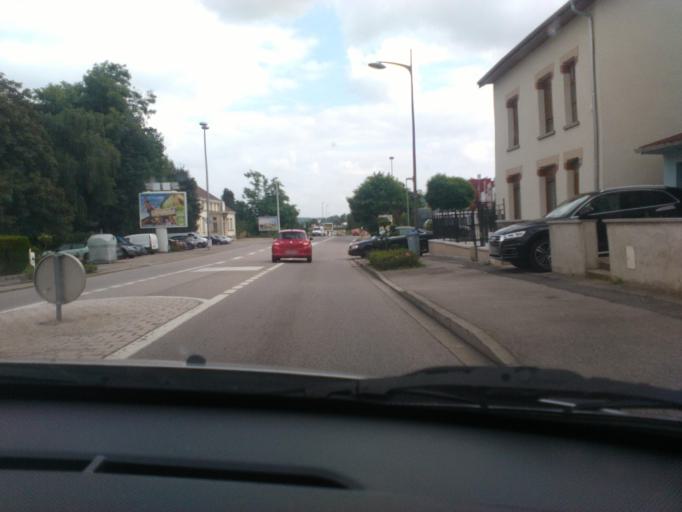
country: FR
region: Lorraine
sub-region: Departement de Meurthe-et-Moselle
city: Champigneulles
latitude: 48.7475
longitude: 6.1499
